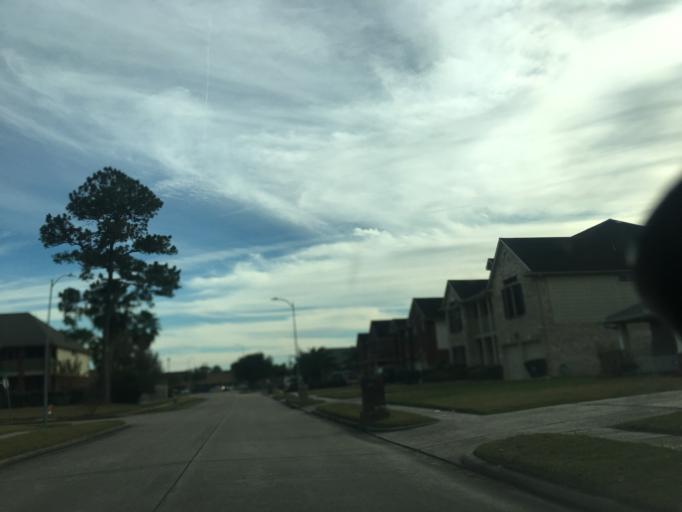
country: US
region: Texas
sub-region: Harris County
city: Cloverleaf
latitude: 29.8092
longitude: -95.1692
